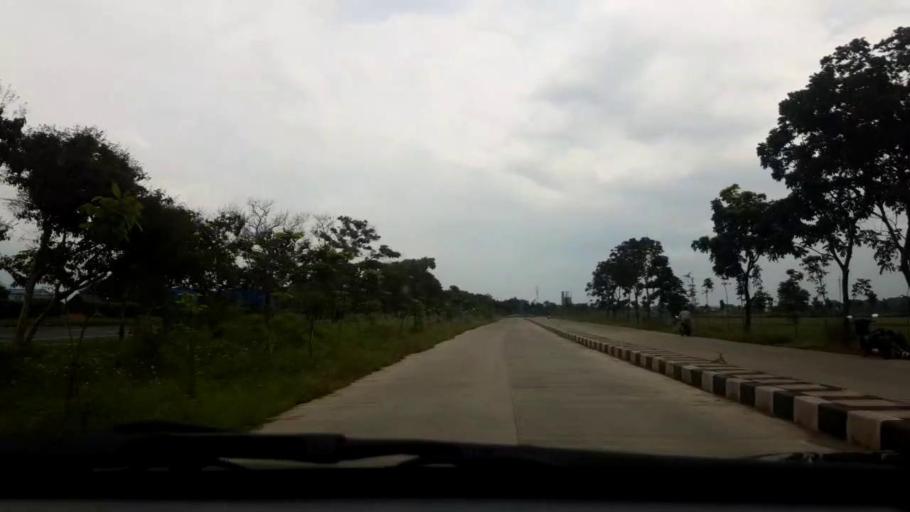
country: ID
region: West Java
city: Cileunyi
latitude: -6.9635
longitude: 107.7119
